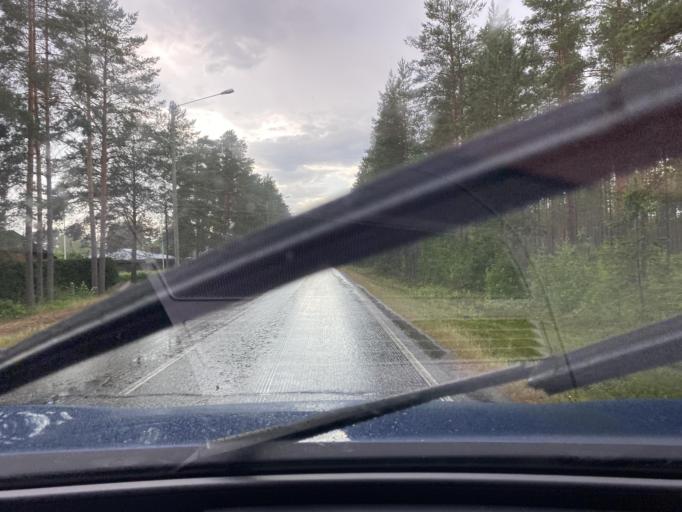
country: FI
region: Central Ostrobothnia
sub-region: Kaustinen
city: Veteli
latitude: 63.4693
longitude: 23.8212
